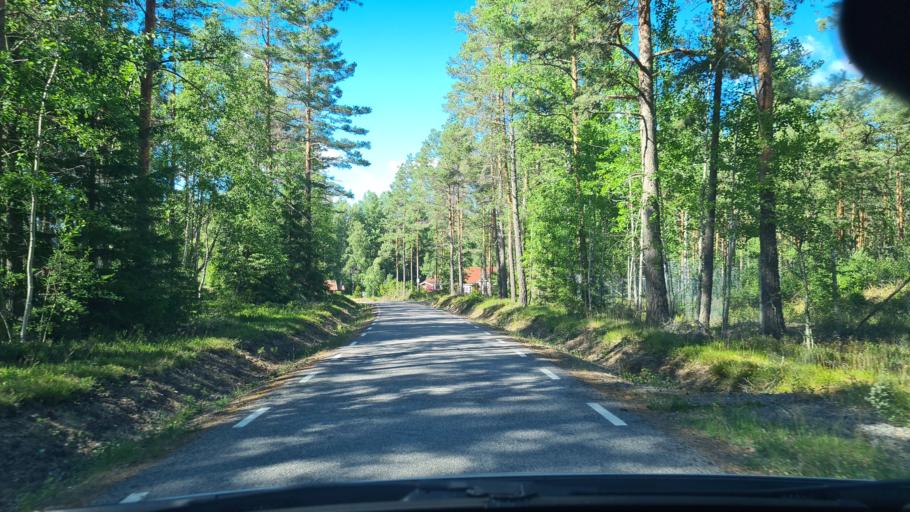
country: SE
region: OEstergoetland
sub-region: Norrkopings Kommun
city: Krokek
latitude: 58.7138
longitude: 16.4292
